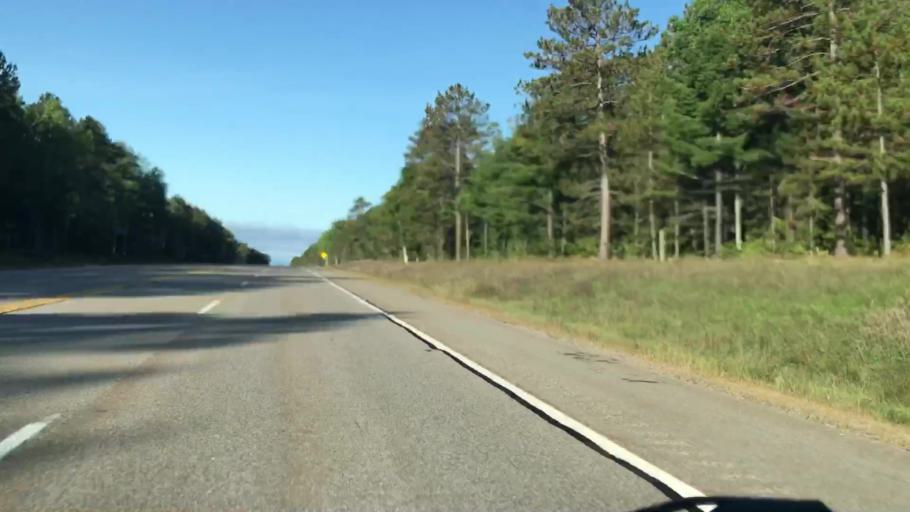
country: US
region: Michigan
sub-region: Chippewa County
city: Sault Ste. Marie
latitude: 46.3636
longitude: -84.7689
